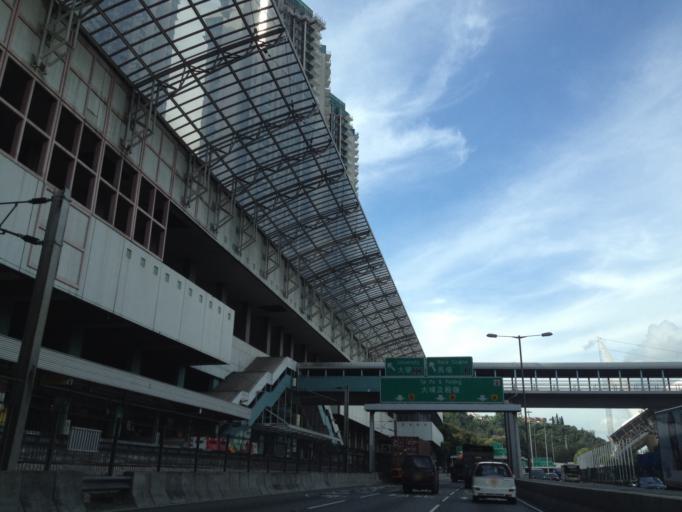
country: HK
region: Sha Tin
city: Sha Tin
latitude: 22.4003
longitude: 114.2031
